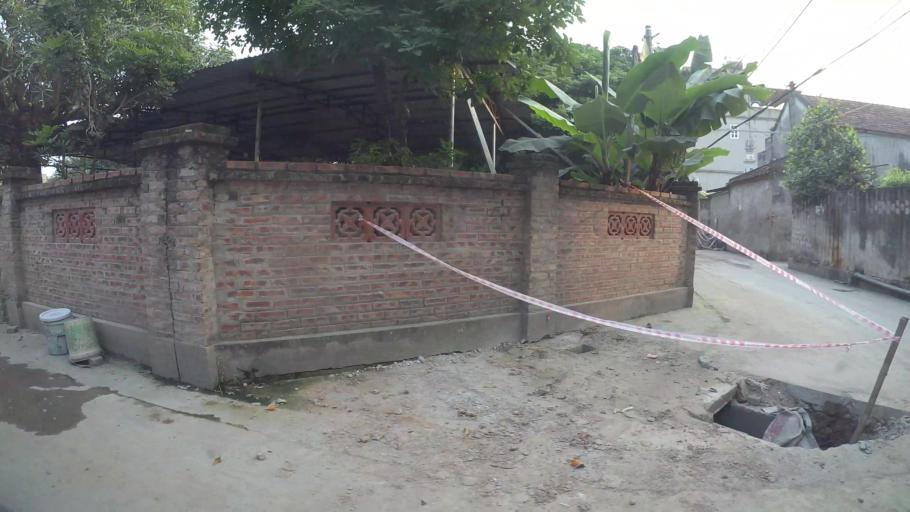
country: VN
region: Ha Noi
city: Cau Dien
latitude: 21.0063
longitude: 105.7238
